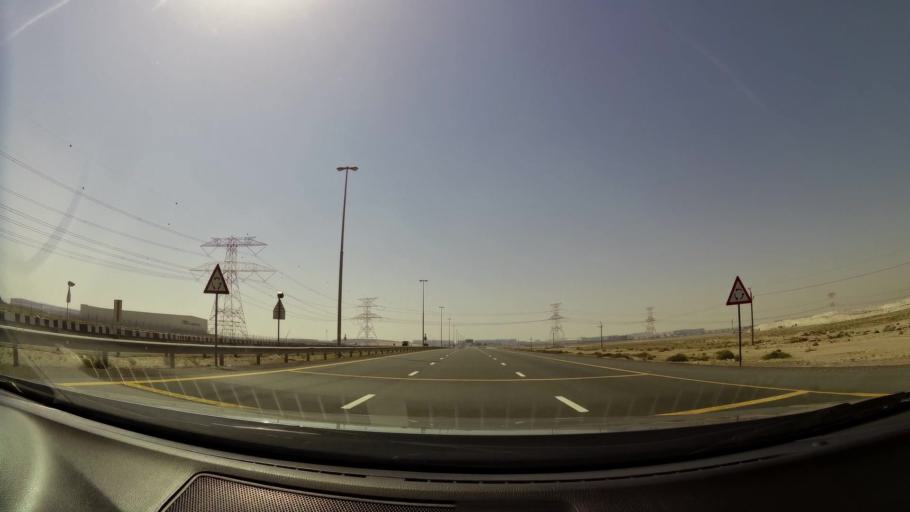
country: AE
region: Dubai
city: Dubai
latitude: 24.9251
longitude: 55.0950
